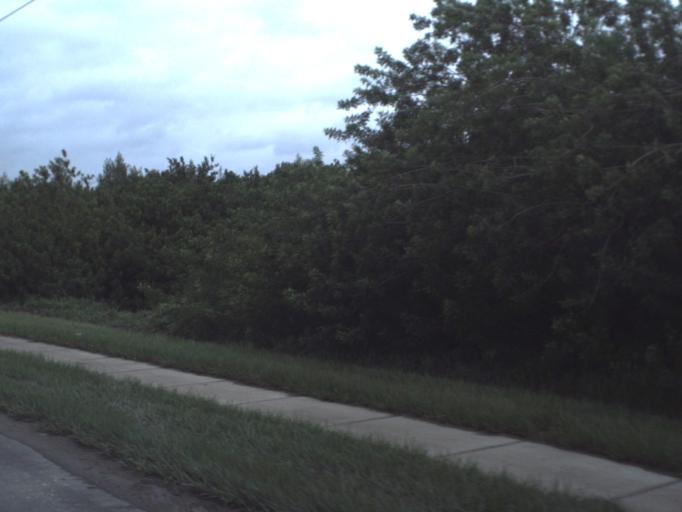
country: US
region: Florida
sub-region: Hillsborough County
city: Tampa
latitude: 27.9280
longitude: -82.4241
